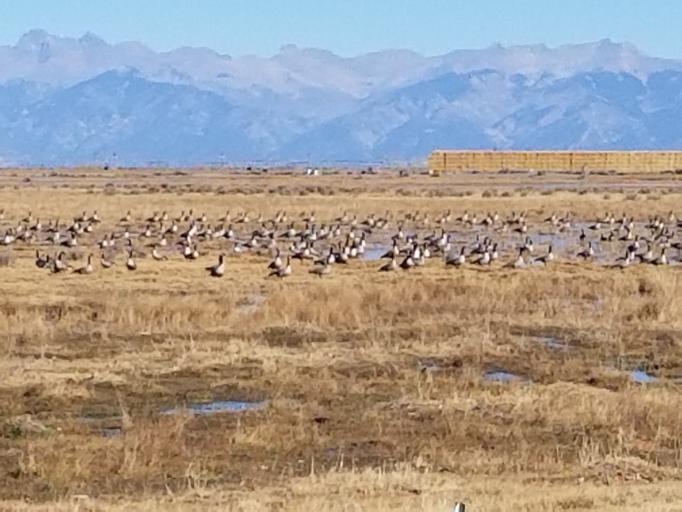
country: US
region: Colorado
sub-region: Rio Grande County
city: Monte Vista
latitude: 37.5742
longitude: -105.9906
